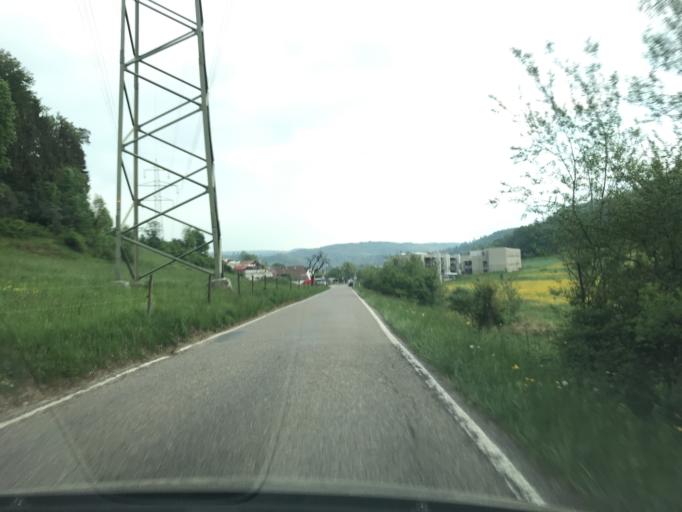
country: CH
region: Zurich
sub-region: Bezirk Winterthur
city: Toess (Kreis 4) / Vorder-Daettnau
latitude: 47.4868
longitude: 8.6892
